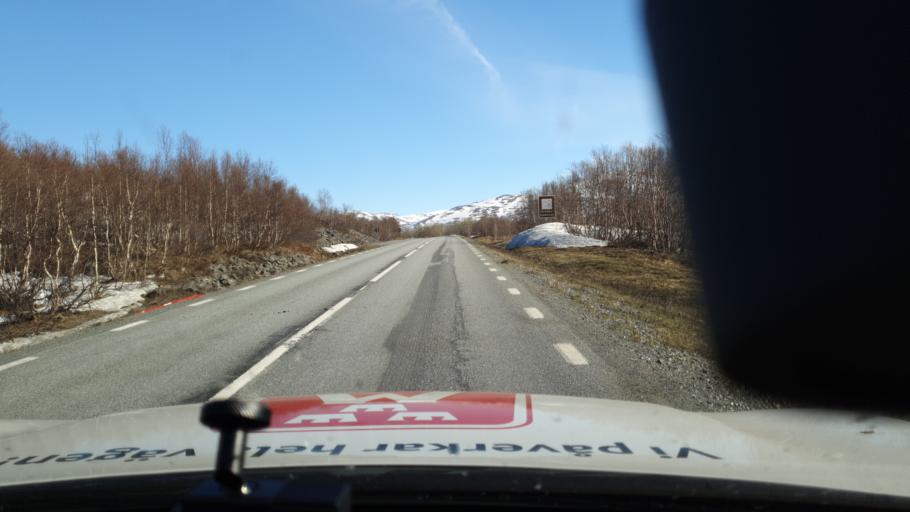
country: NO
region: Nordland
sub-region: Rana
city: Mo i Rana
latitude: 66.1301
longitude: 14.6001
